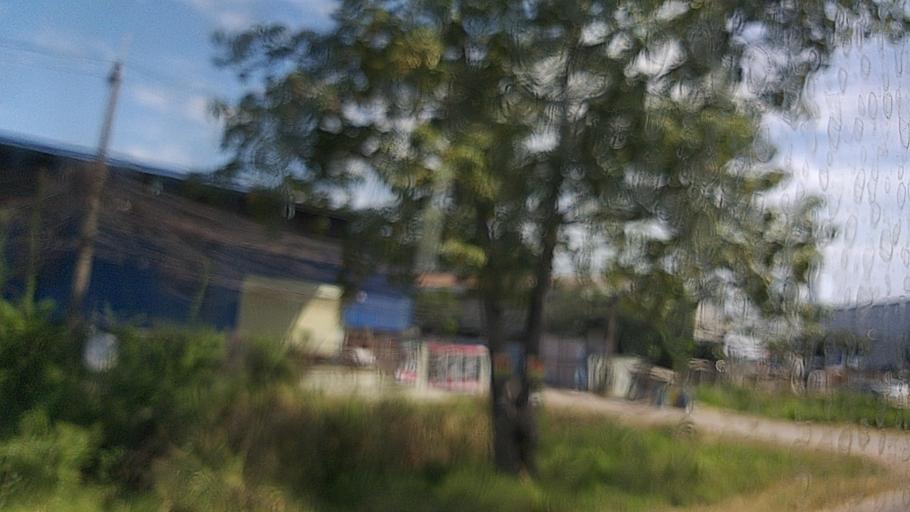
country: TH
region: Khon Kaen
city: Khon Kaen
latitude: 16.3863
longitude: 102.8246
